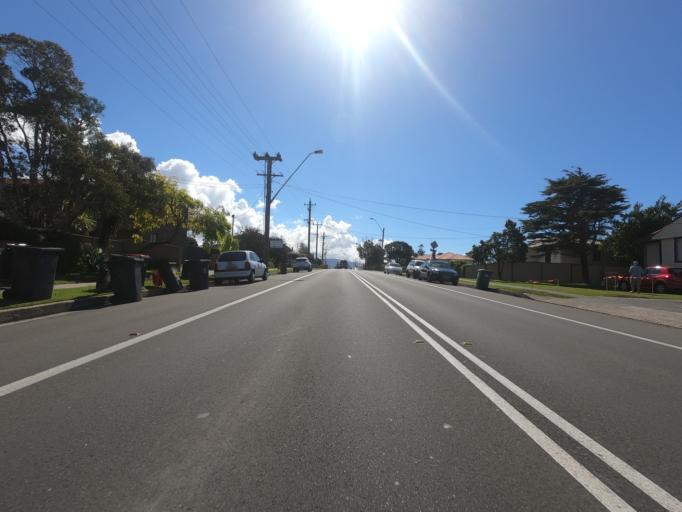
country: AU
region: New South Wales
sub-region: Wollongong
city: East Corrimal
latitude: -34.3701
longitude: 150.9100
